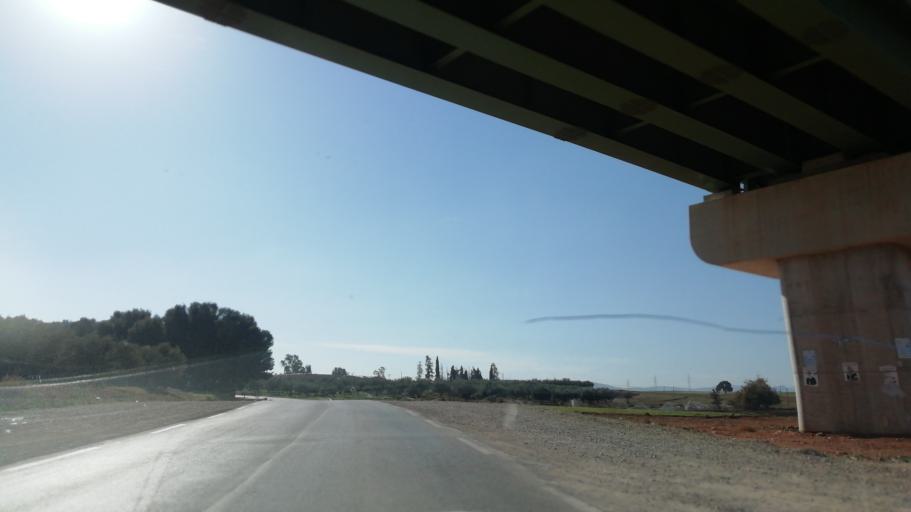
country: DZ
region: Tlemcen
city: Ouled Mimoun
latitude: 35.0066
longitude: -0.9072
